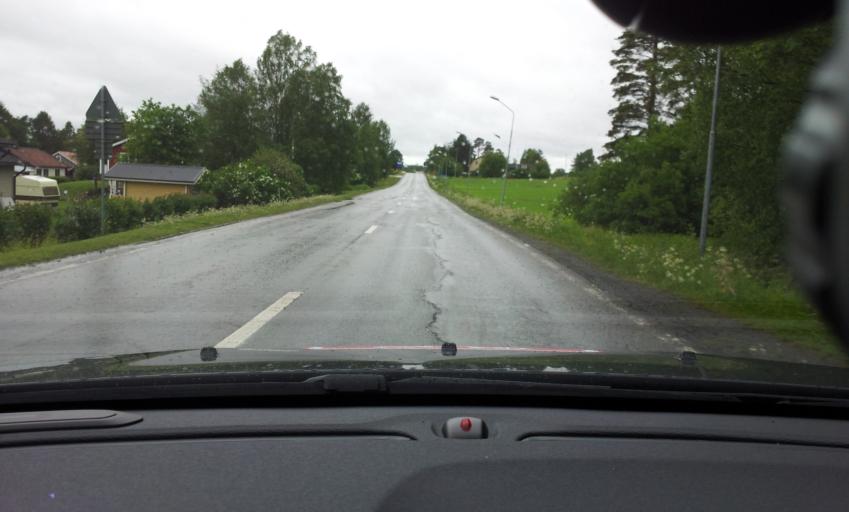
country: SE
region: Jaemtland
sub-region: Krokoms Kommun
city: Krokom
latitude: 63.2994
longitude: 14.4793
